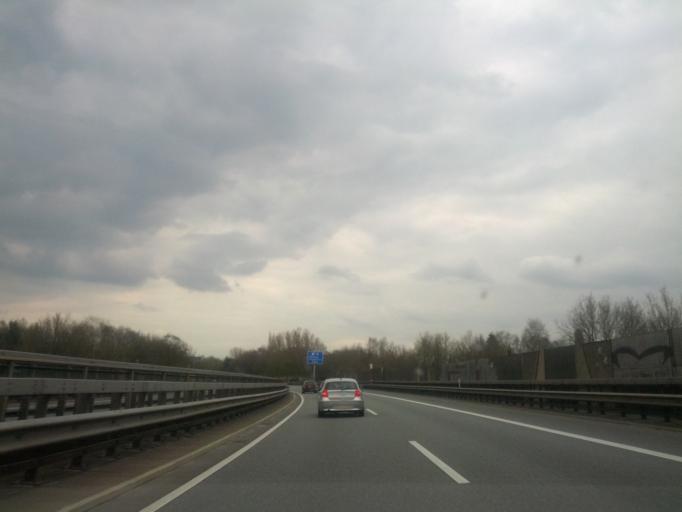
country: DE
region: Lower Saxony
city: Oldenburg
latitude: 53.1311
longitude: 8.1946
